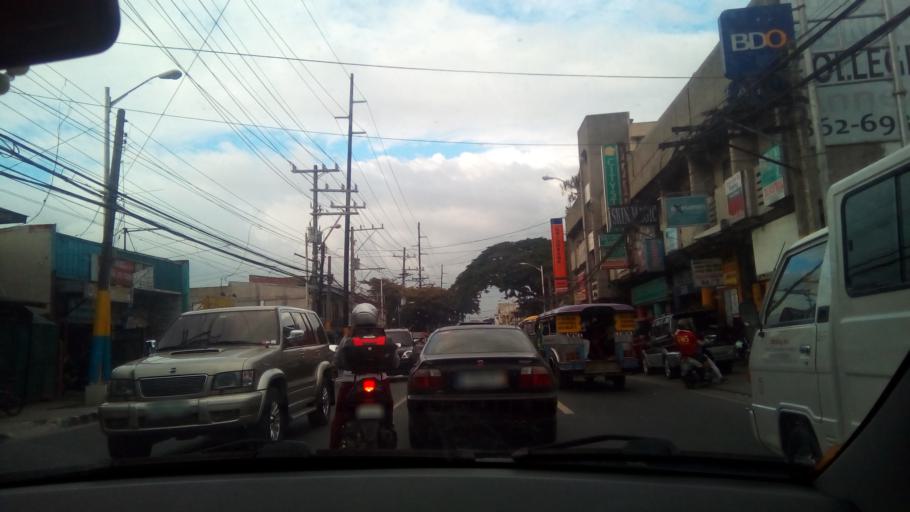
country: PH
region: Calabarzon
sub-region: Province of Laguna
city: San Pedro
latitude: 14.3912
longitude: 121.0445
